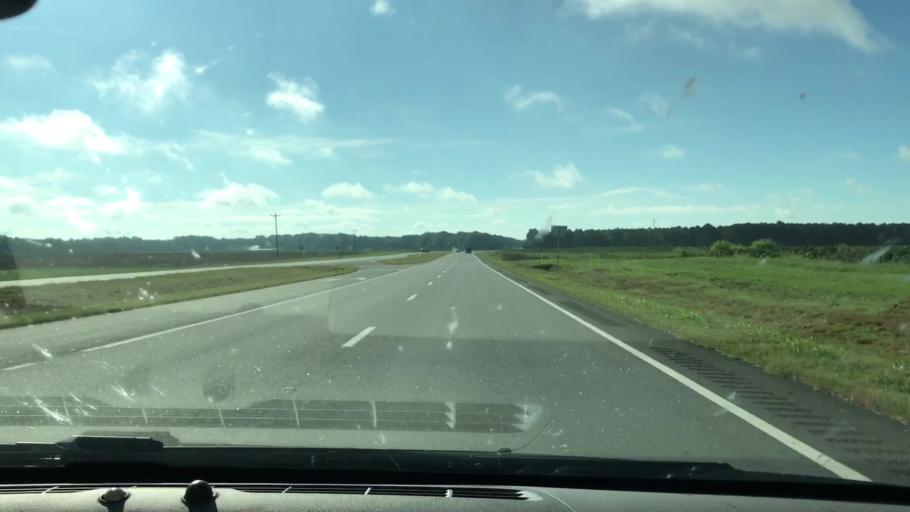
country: US
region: Georgia
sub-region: Terrell County
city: Dawson
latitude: 31.7001
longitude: -84.3246
